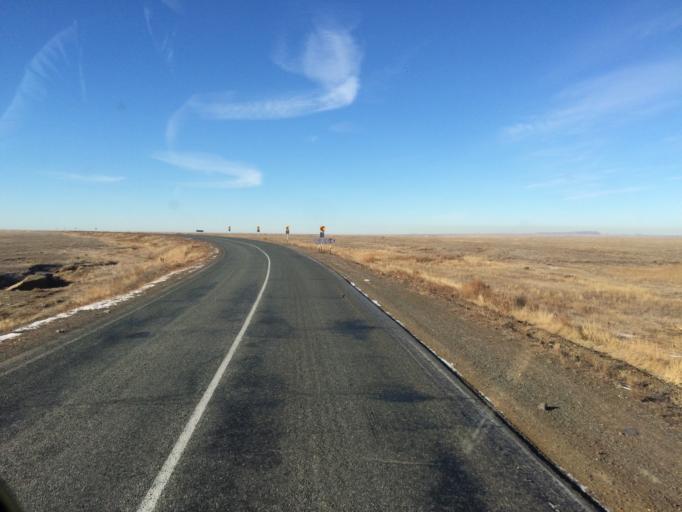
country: KZ
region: Aqtoebe
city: Khromtau
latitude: 50.1858
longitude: 58.6697
